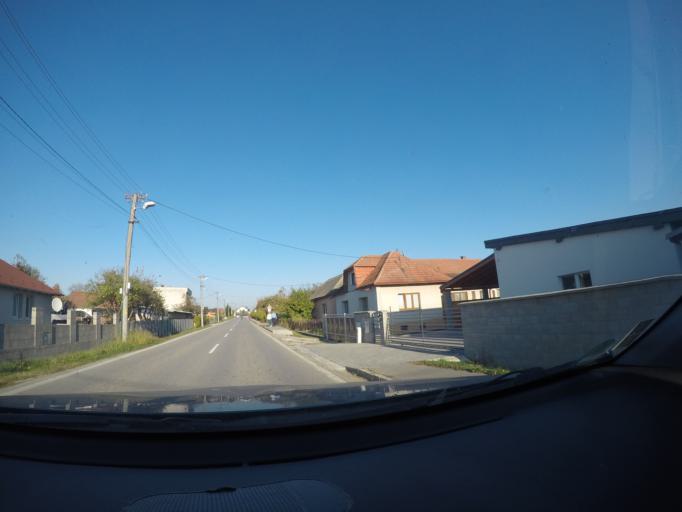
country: SK
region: Nitriansky
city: Nemsova
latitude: 48.9586
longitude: 18.1039
